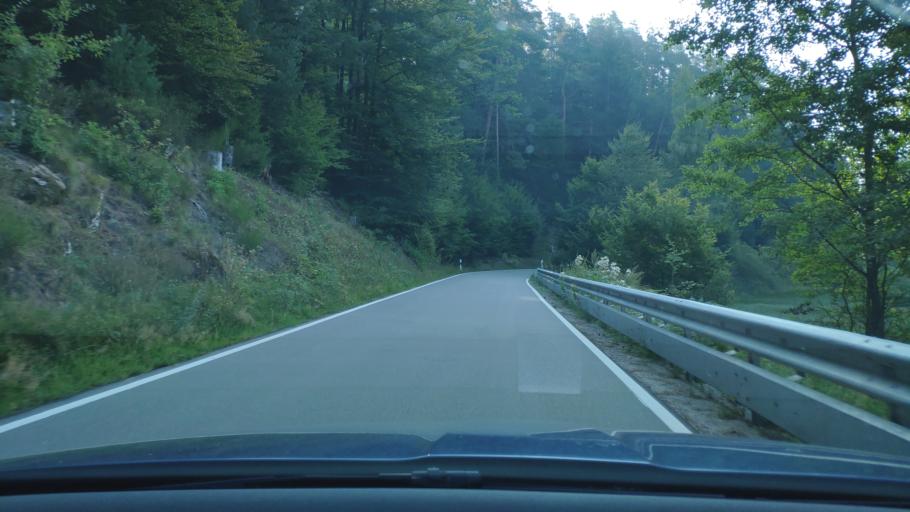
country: DE
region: Rheinland-Pfalz
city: Ludwigswinkel
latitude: 49.1030
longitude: 7.6212
